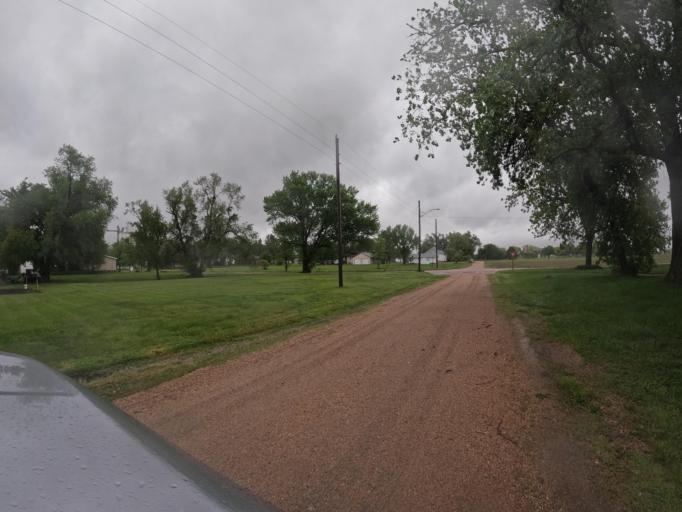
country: US
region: Nebraska
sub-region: Clay County
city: Harvard
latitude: 40.6134
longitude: -98.0978
